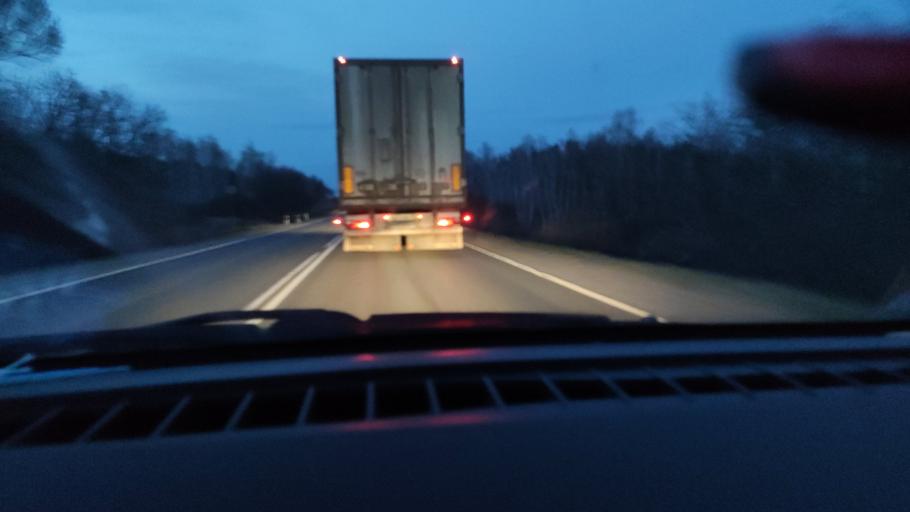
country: RU
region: Saratov
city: Sennoy
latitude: 52.1186
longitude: 46.8420
